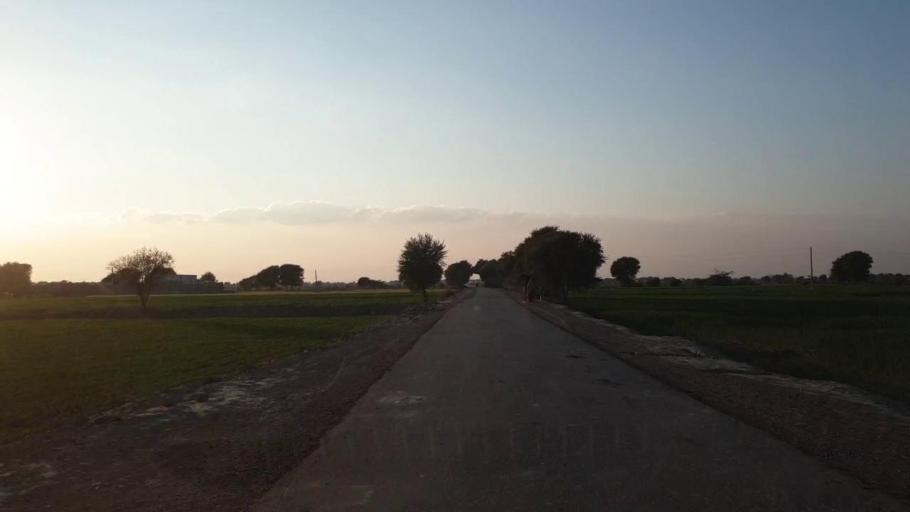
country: PK
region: Sindh
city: Shahpur Chakar
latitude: 26.1561
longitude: 68.5555
